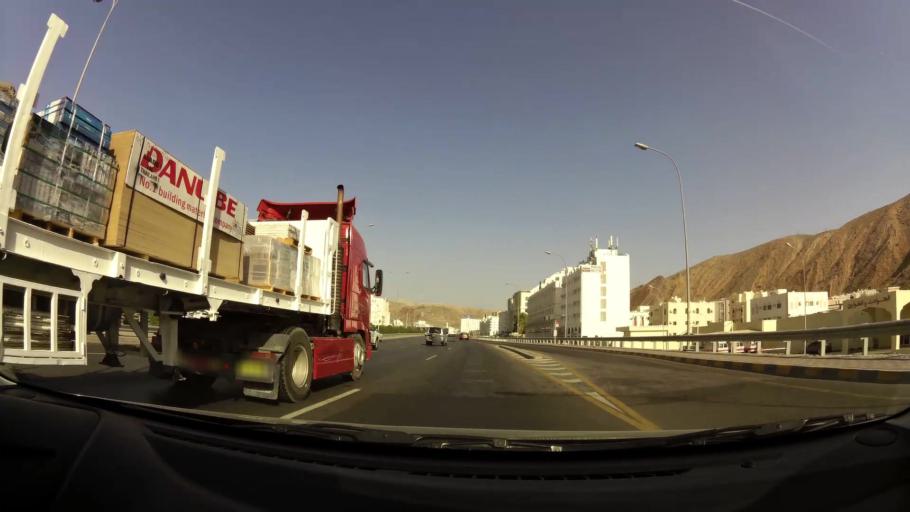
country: OM
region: Muhafazat Masqat
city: Muscat
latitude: 23.5888
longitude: 58.5333
